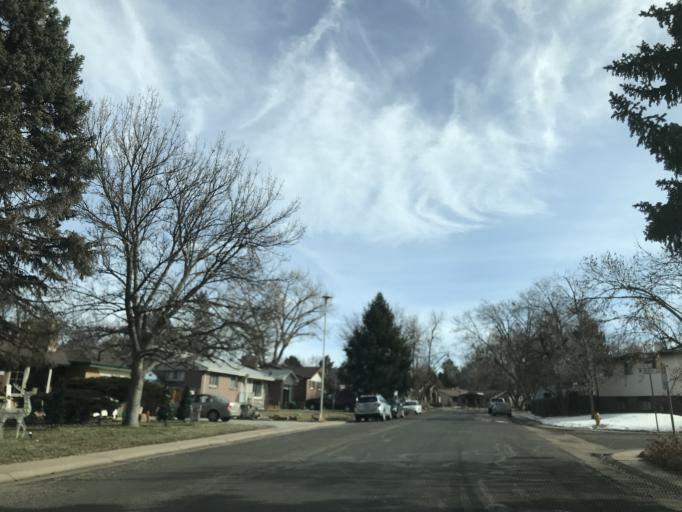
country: US
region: Colorado
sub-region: Arapahoe County
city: Columbine Valley
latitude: 39.5944
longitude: -105.0159
